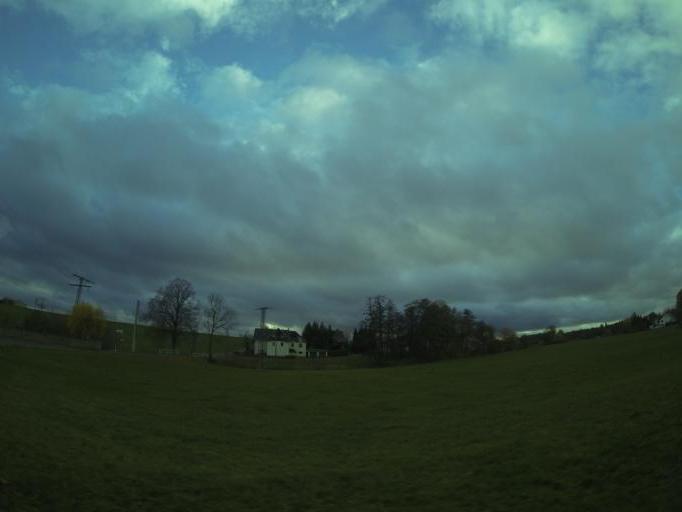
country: DE
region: Thuringia
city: Vollmershain
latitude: 50.8501
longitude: 12.3099
